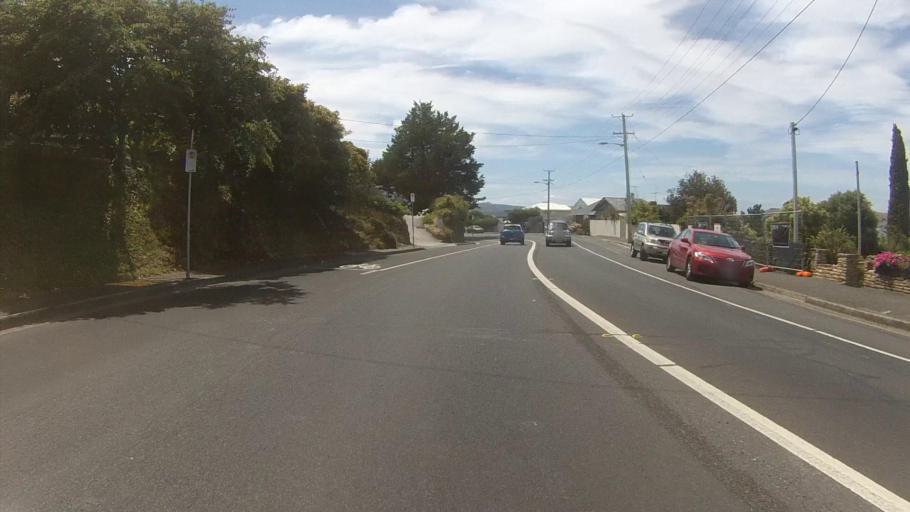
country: AU
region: Tasmania
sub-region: Kingborough
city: Taroona
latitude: -42.9282
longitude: 147.3599
